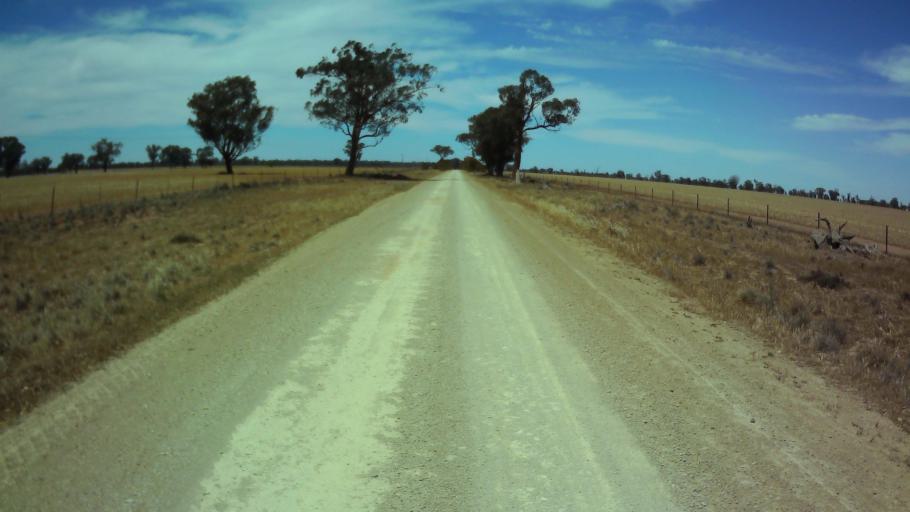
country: AU
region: New South Wales
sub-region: Weddin
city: Grenfell
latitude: -33.8756
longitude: 147.8055
